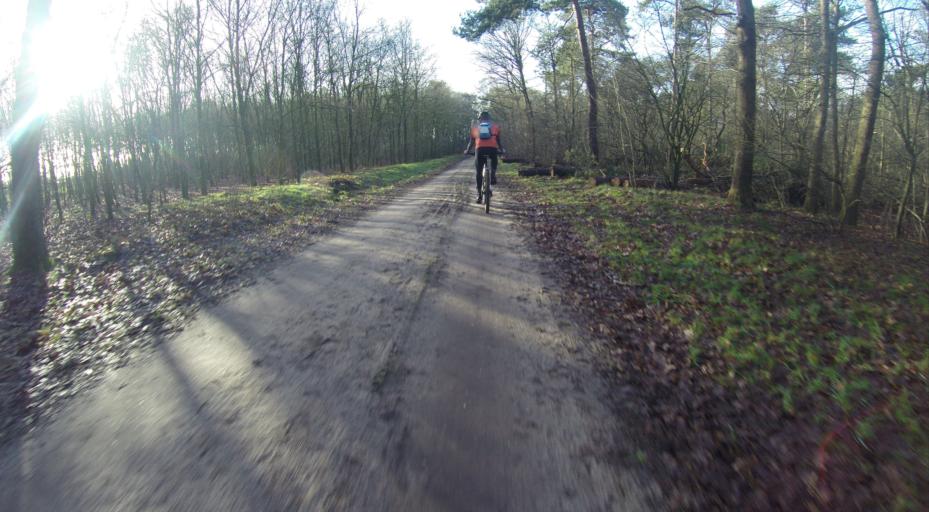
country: NL
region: Gelderland
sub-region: Gemeente Lochem
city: Laren
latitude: 52.3182
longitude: 6.3898
